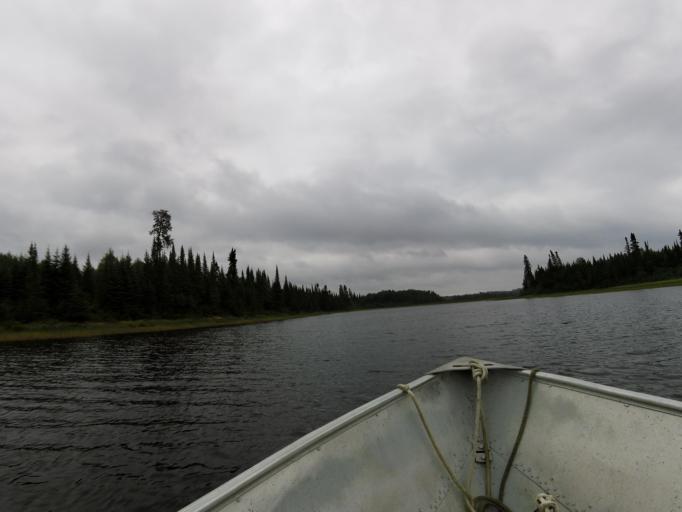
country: CA
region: Ontario
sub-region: Rainy River District
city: Atikokan
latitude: 49.5954
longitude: -91.3398
